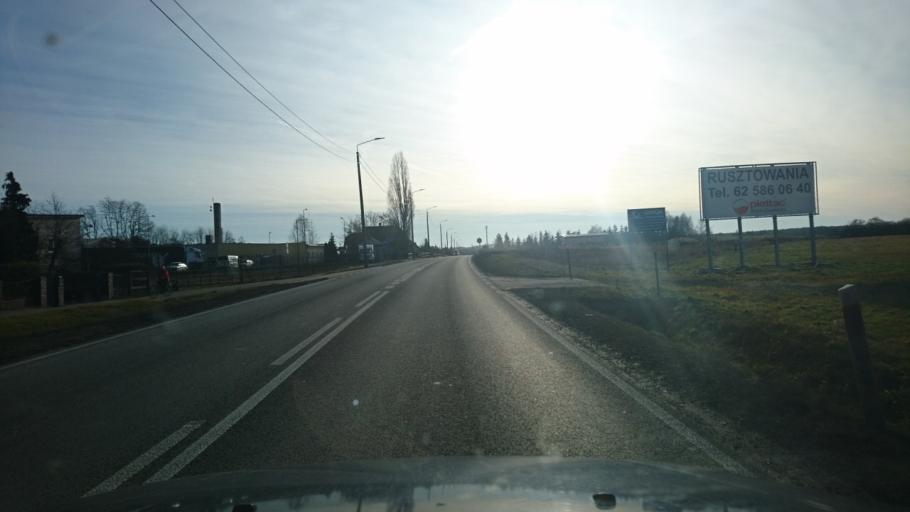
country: PL
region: Greater Poland Voivodeship
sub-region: Powiat ostrzeszowski
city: Ostrzeszow
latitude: 51.4421
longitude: 17.9137
